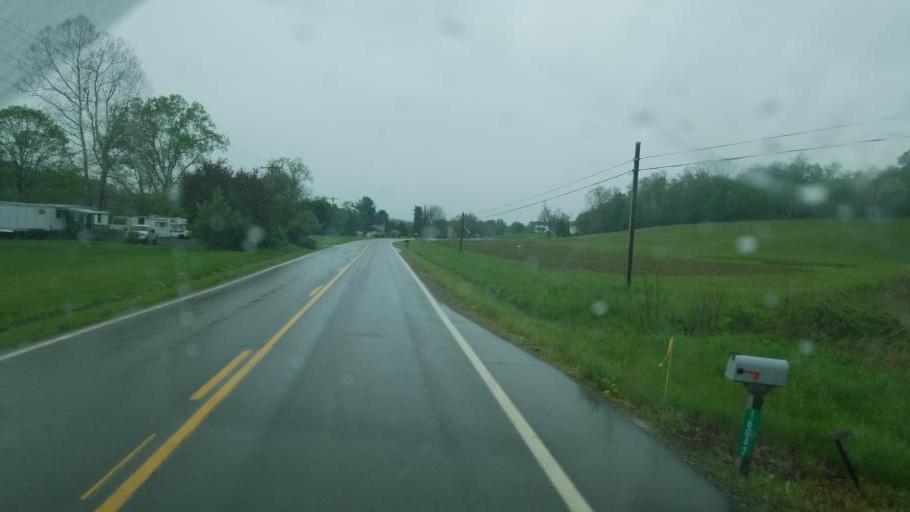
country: US
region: Ohio
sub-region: Muskingum County
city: Dresden
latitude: 40.1928
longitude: -82.0422
